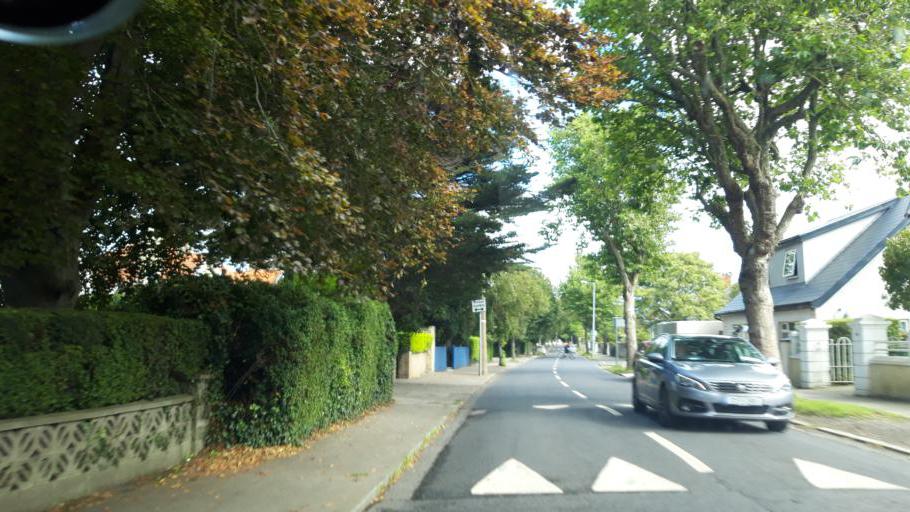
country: IE
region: Leinster
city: Dollymount
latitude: 53.3636
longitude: -6.1894
